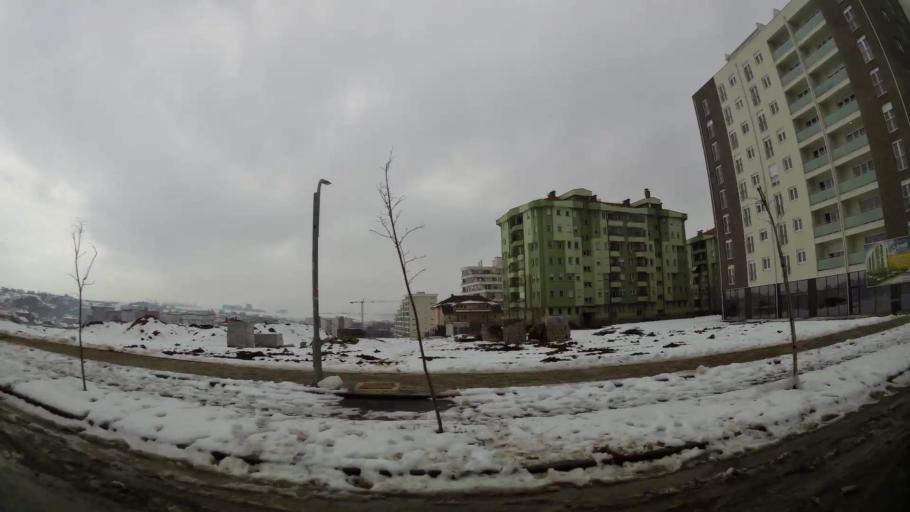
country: XK
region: Pristina
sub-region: Komuna e Prishtines
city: Pristina
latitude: 42.6502
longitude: 21.1787
